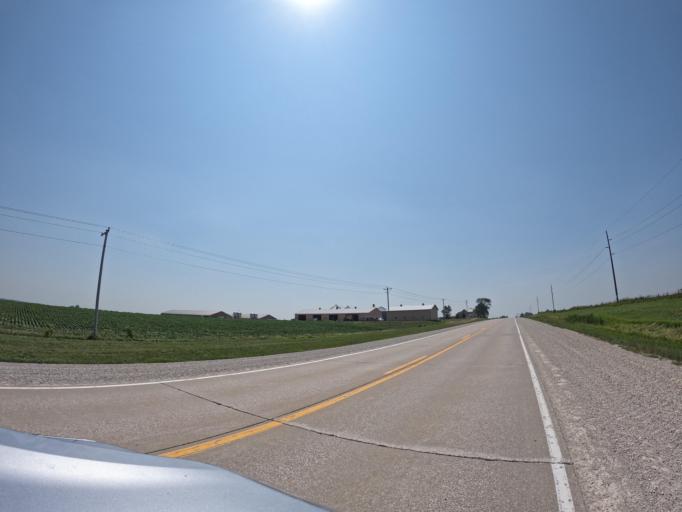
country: US
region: Iowa
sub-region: Keokuk County
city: Sigourney
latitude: 41.3369
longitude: -92.2488
